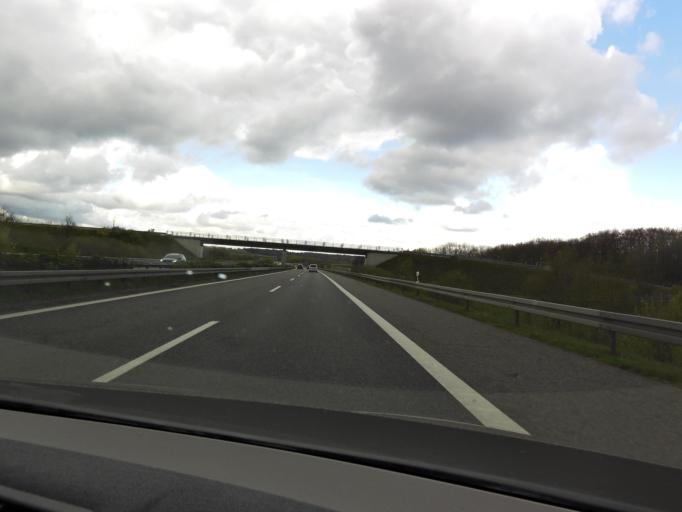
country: DE
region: Mecklenburg-Vorpommern
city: Tessin
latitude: 54.0267
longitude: 12.4192
